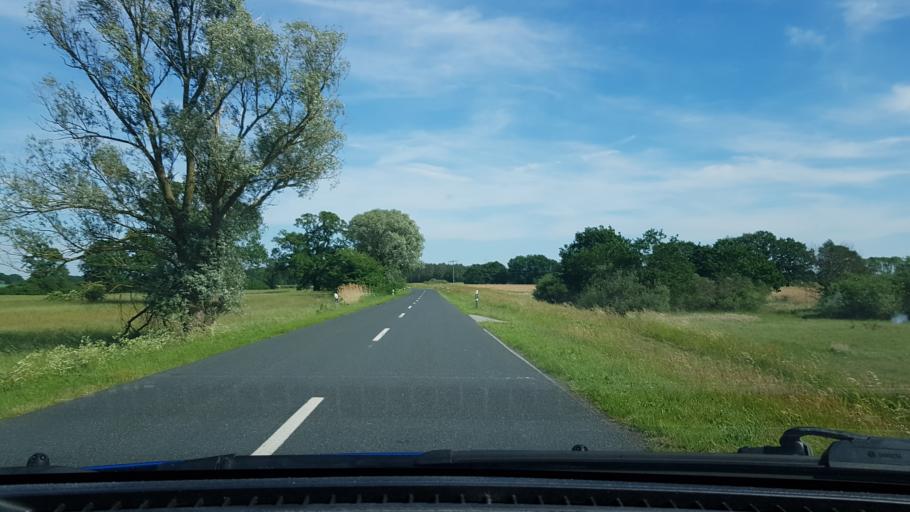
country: DE
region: Lower Saxony
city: Neu Darchau
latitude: 53.3304
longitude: 10.8833
